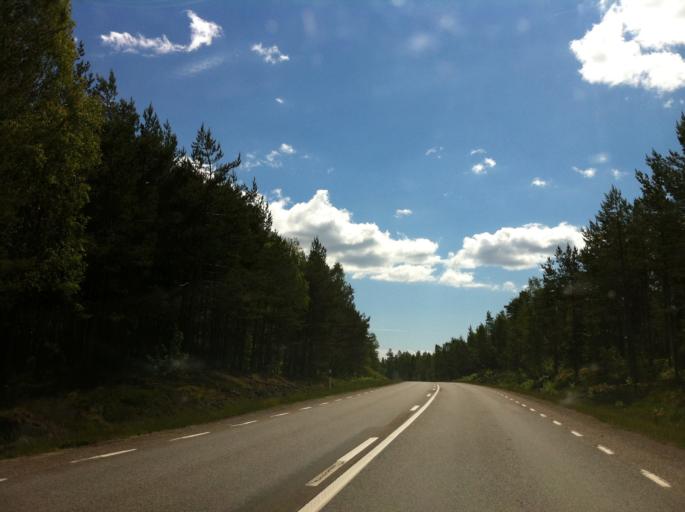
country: SE
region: Vaestra Goetaland
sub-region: Amals Kommun
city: Amal
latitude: 59.0275
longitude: 12.6735
